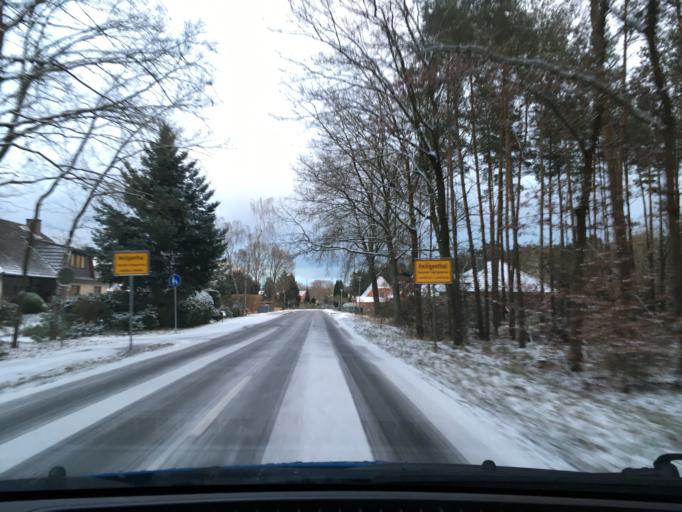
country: DE
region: Lower Saxony
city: Sudergellersen
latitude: 53.2213
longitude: 10.3307
